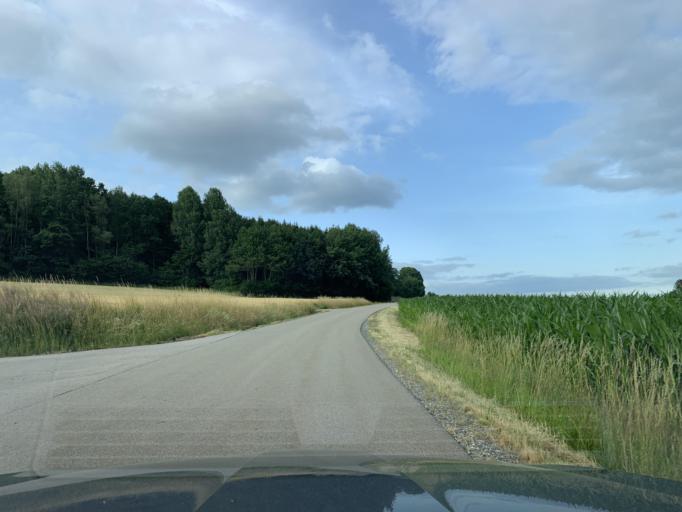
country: DE
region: Bavaria
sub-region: Upper Palatinate
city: Dieterskirchen
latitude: 49.4055
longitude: 12.4430
